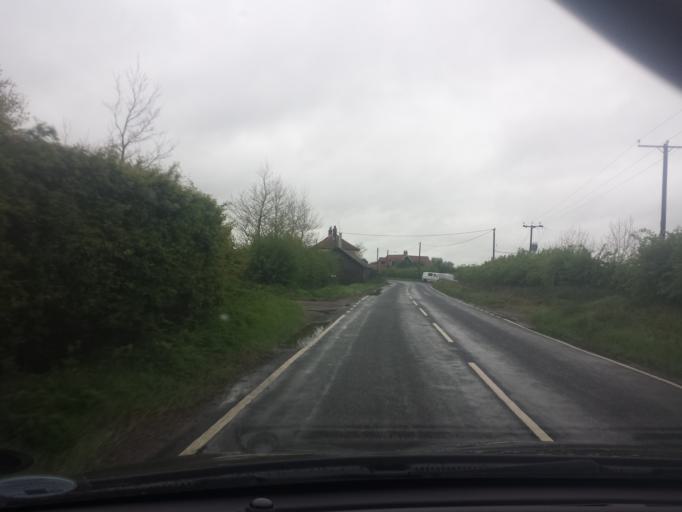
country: GB
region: England
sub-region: Essex
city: Alresford
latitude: 51.9006
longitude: 1.0132
